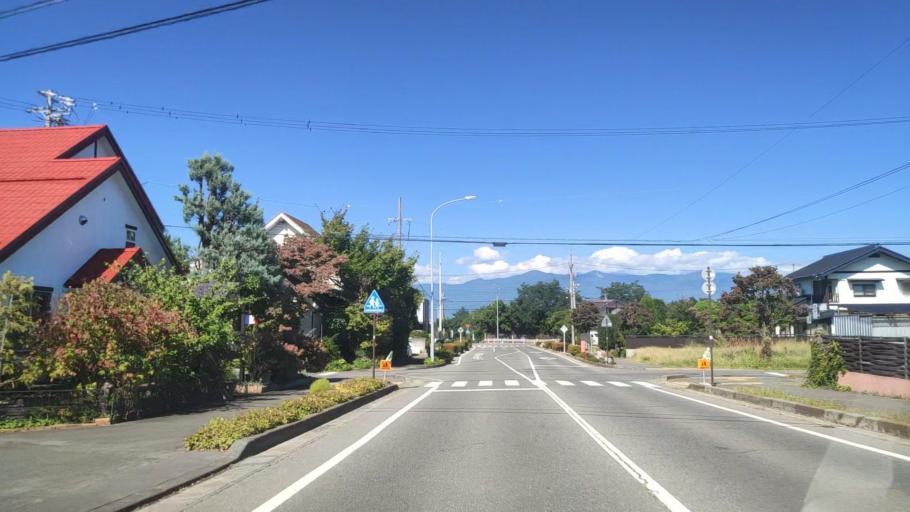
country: JP
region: Nagano
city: Shiojiri
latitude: 36.1590
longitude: 137.9454
